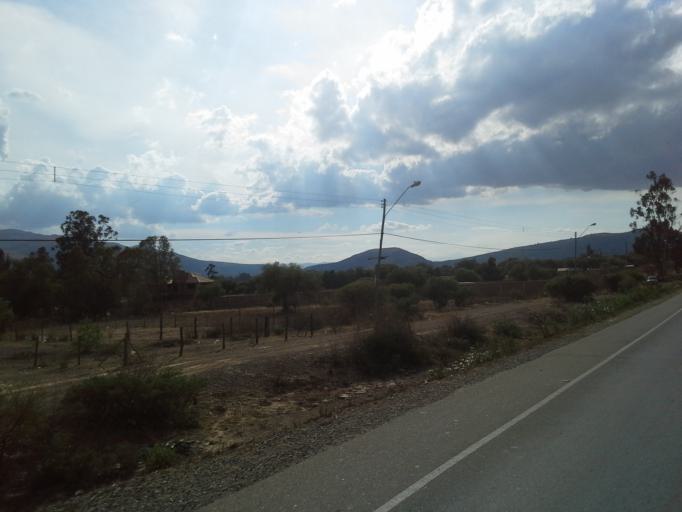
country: BO
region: Cochabamba
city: Tarata
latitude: -17.5401
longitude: -66.0654
